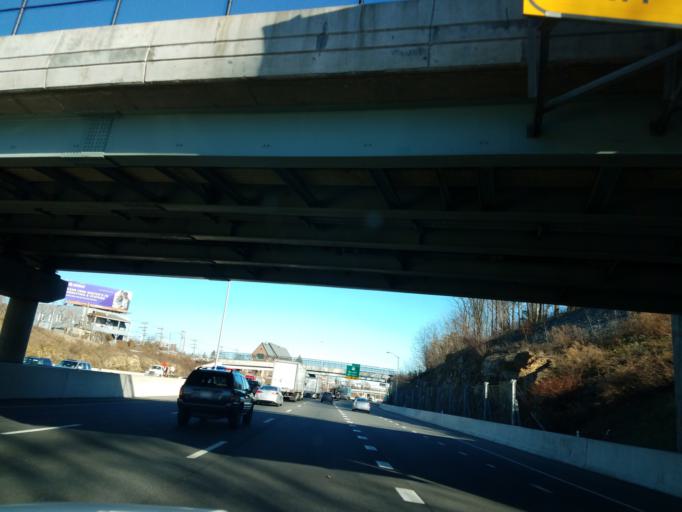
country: US
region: Connecticut
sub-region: Fairfield County
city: Norwalk
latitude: 41.1037
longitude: -73.4301
